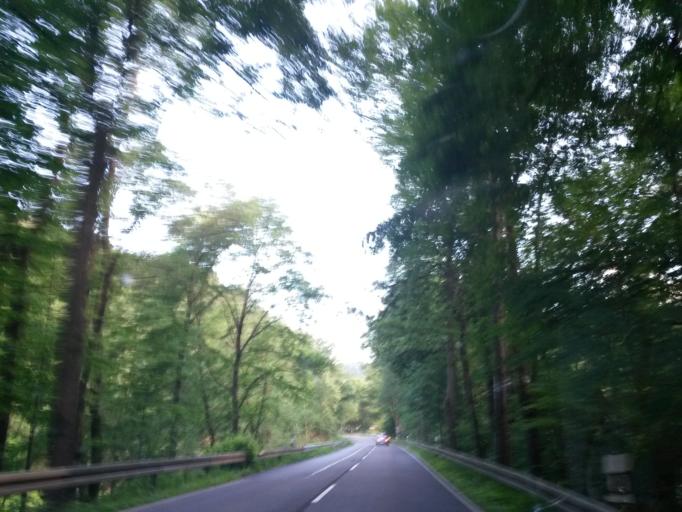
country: DE
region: North Rhine-Westphalia
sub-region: Regierungsbezirk Koln
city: Overath
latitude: 50.9182
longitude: 7.3263
